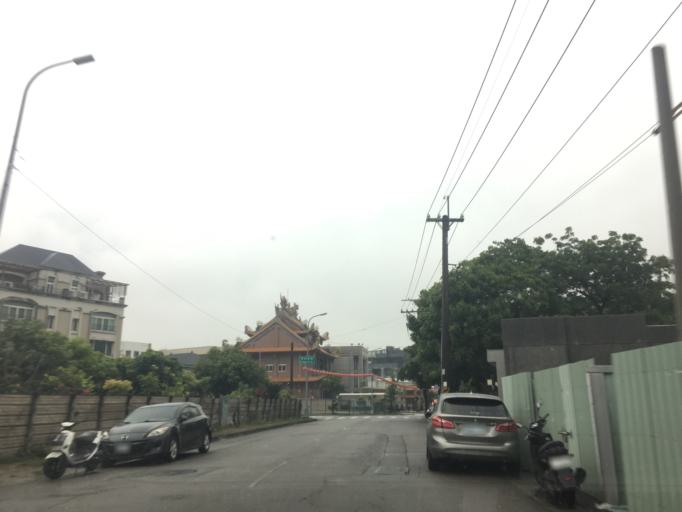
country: TW
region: Taiwan
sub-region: Taichung City
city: Taichung
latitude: 24.1687
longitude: 120.7128
